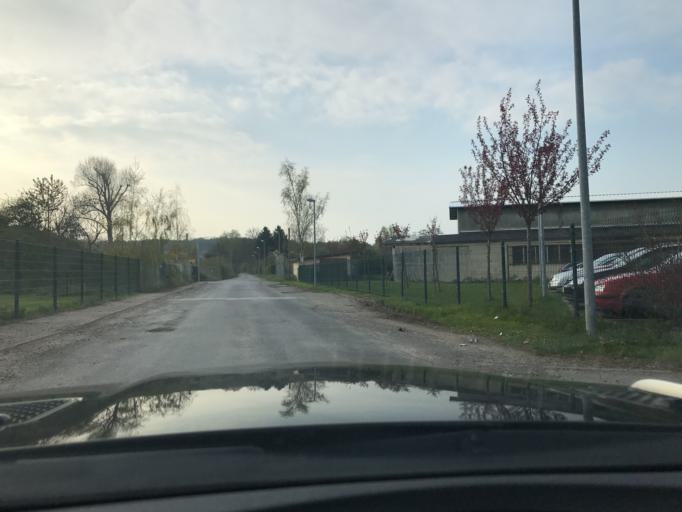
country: DE
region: Thuringia
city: Muehlhausen
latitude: 51.2097
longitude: 10.4781
